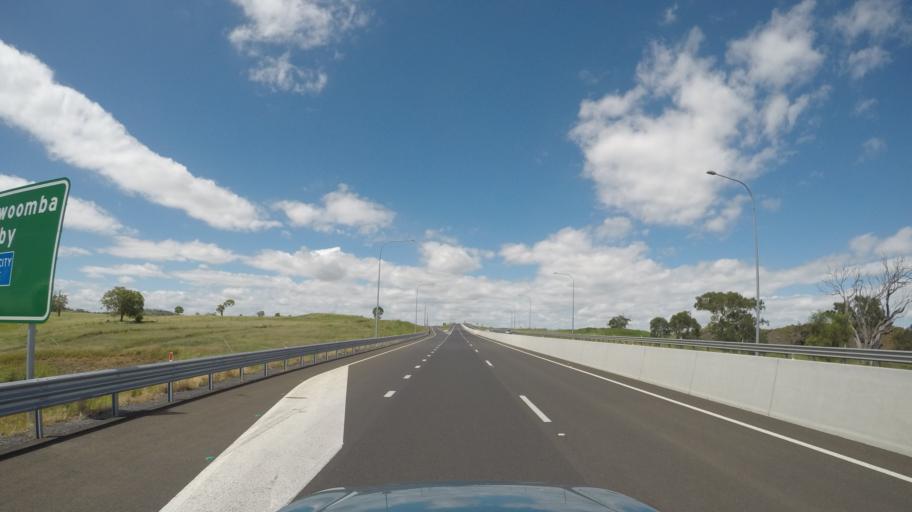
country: AU
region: Queensland
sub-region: Toowoomba
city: Wilsonton Heights
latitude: -27.5174
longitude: 151.8651
